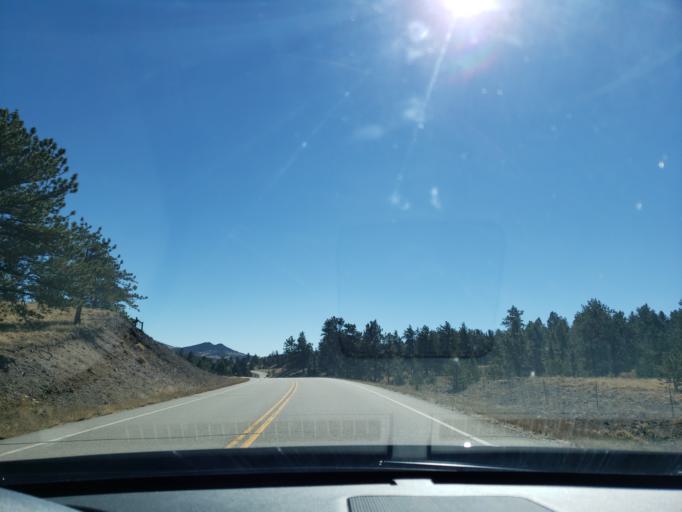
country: US
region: Colorado
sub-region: Chaffee County
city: Buena Vista
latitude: 38.8818
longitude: -105.6792
